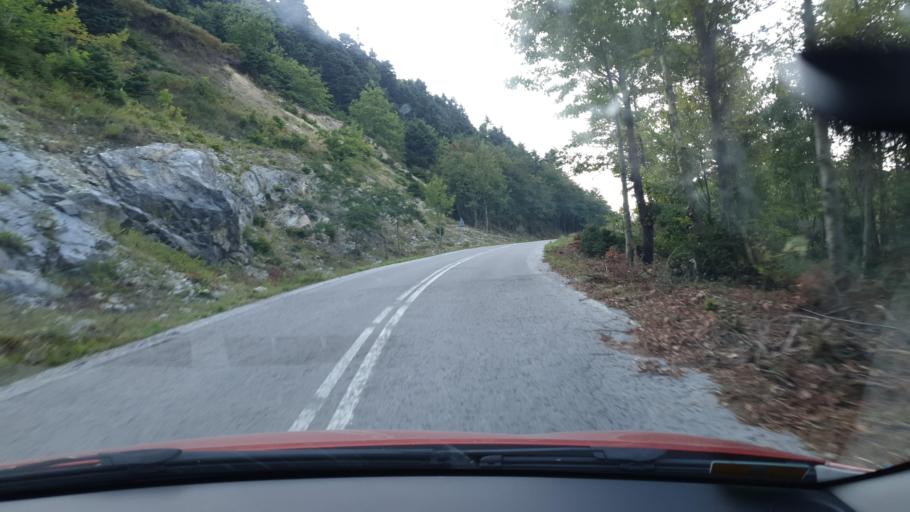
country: GR
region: Central Greece
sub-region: Nomos Evvoias
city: Yimnon
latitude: 38.5916
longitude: 23.8847
